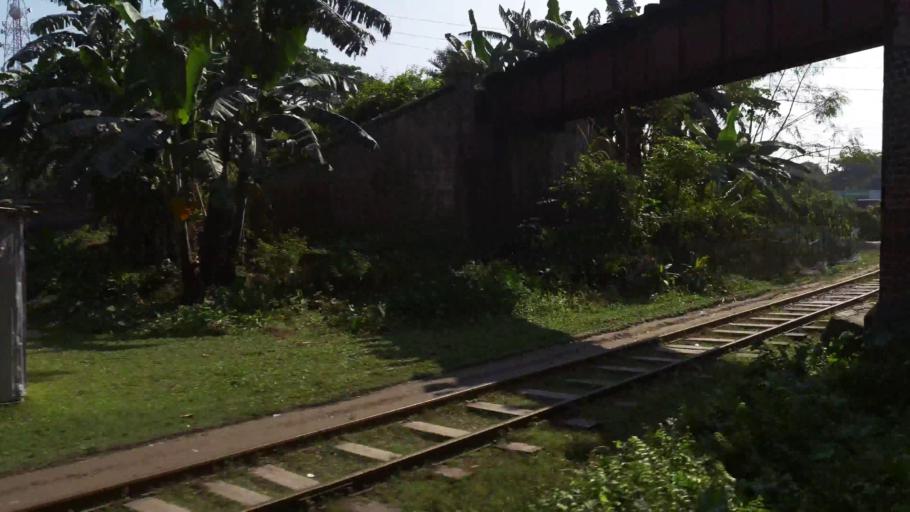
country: BD
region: Dhaka
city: Mymensingh
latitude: 24.6112
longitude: 90.4836
